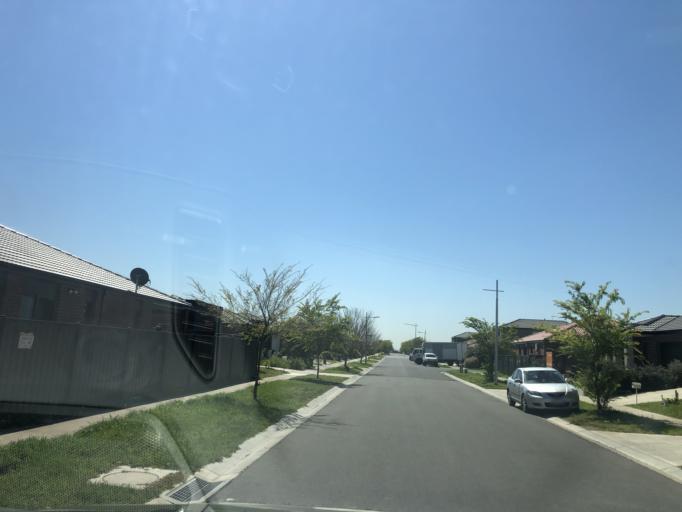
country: AU
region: Victoria
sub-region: Wyndham
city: Point Cook
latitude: -37.9053
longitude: 144.7340
